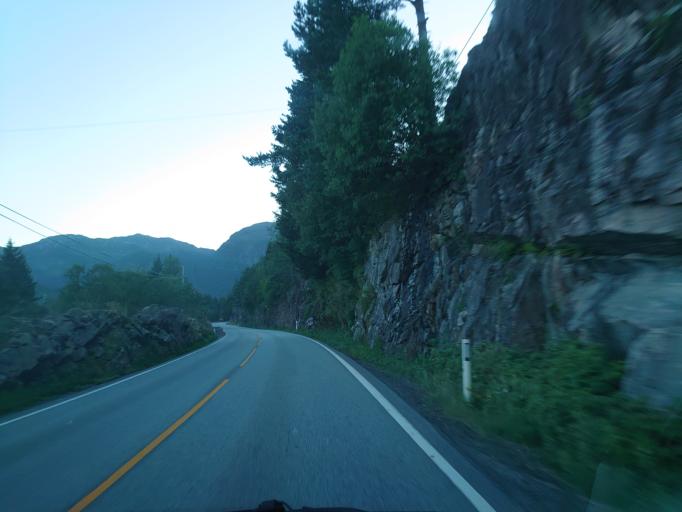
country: NO
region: Hordaland
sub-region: Osteroy
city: Lonevag
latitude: 60.7030
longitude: 5.6025
